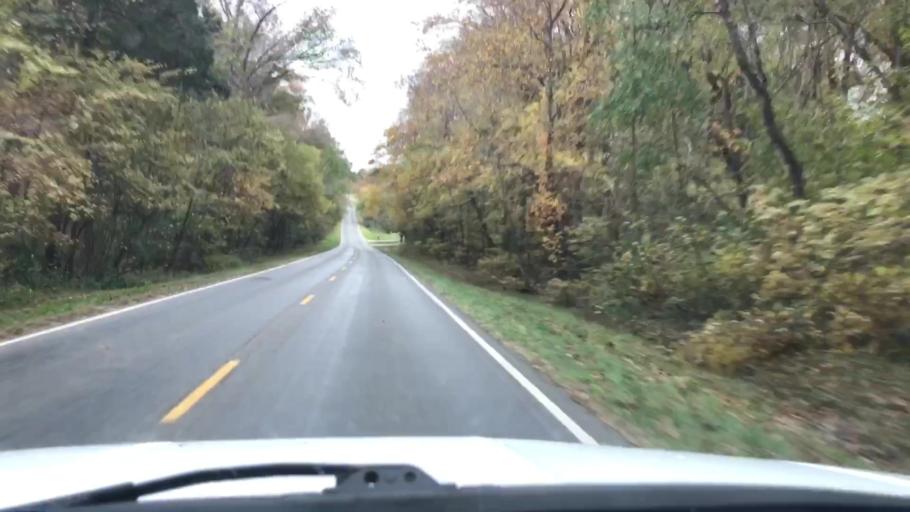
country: US
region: Virginia
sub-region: Goochland County
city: Goochland
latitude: 37.6555
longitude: -77.8538
